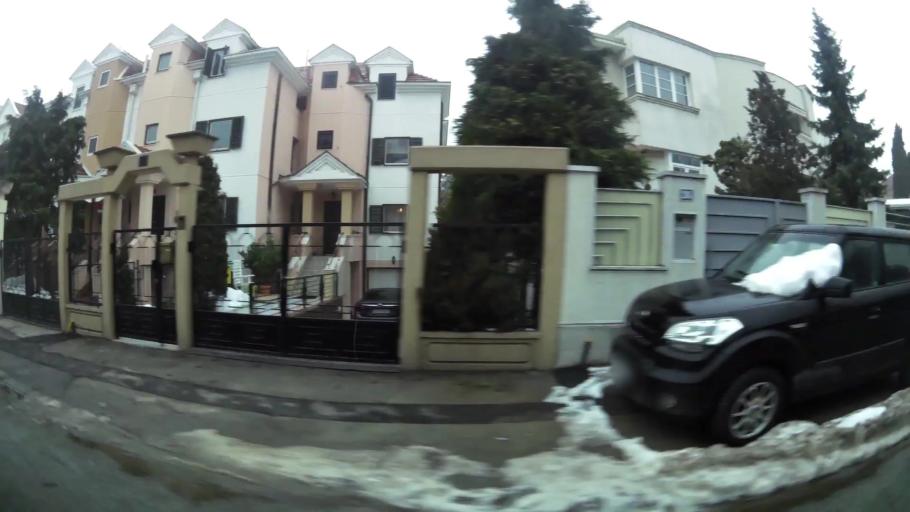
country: RS
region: Central Serbia
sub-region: Belgrade
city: Cukarica
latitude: 44.7906
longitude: 20.4334
